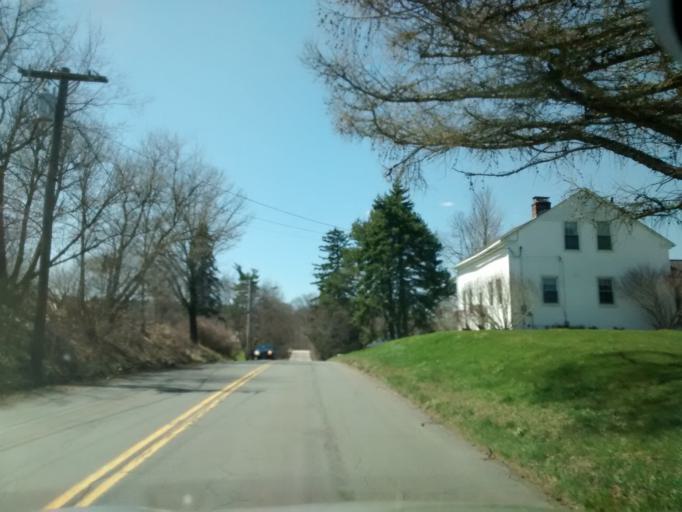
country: US
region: Massachusetts
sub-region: Worcester County
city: Sutton
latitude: 42.1127
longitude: -71.8035
